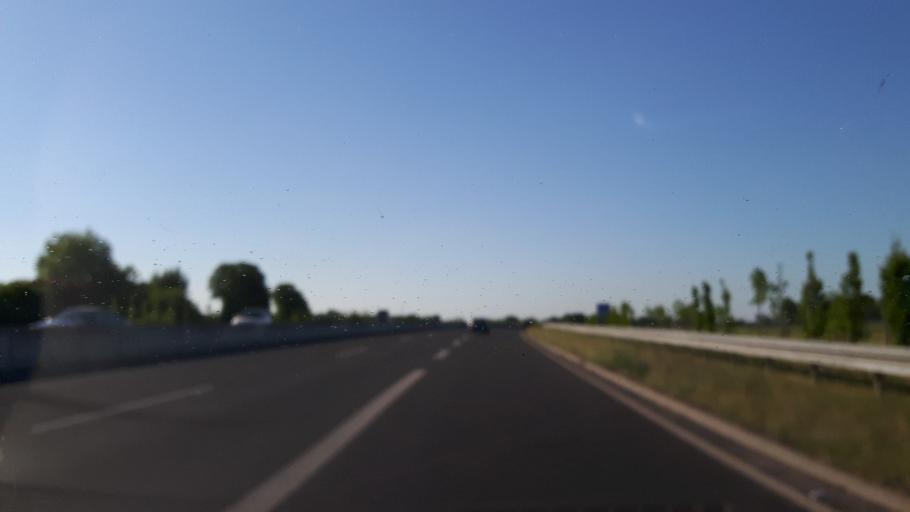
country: DE
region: North Rhine-Westphalia
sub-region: Regierungsbezirk Dusseldorf
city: Hochfeld
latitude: 51.3405
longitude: 6.7516
